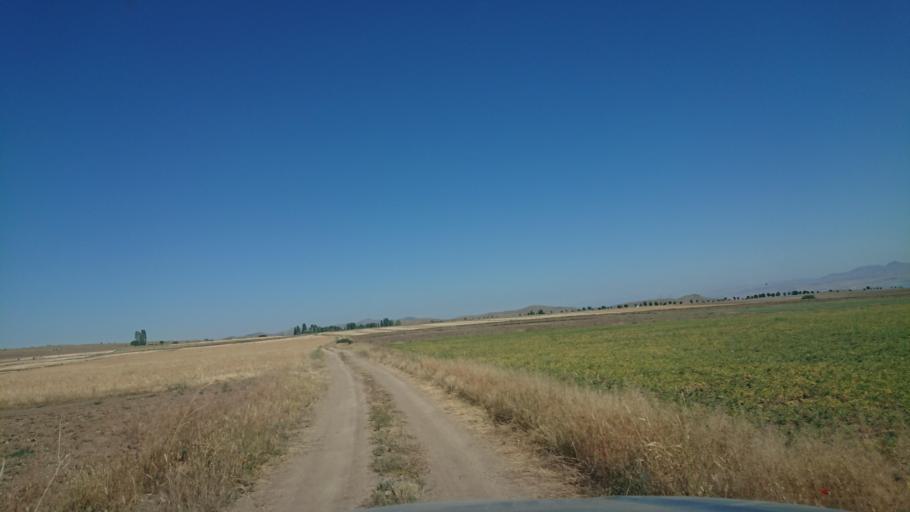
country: TR
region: Aksaray
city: Sariyahsi
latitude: 38.9376
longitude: 33.8392
